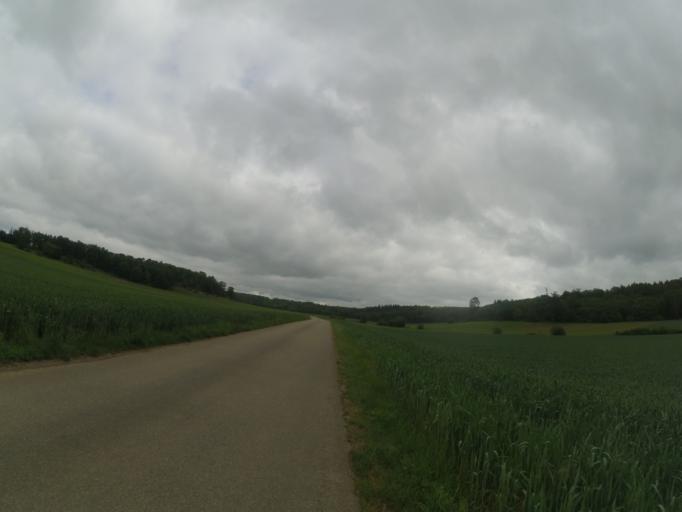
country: DE
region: Baden-Wuerttemberg
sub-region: Tuebingen Region
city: Bernstadt
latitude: 48.5099
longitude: 10.0304
